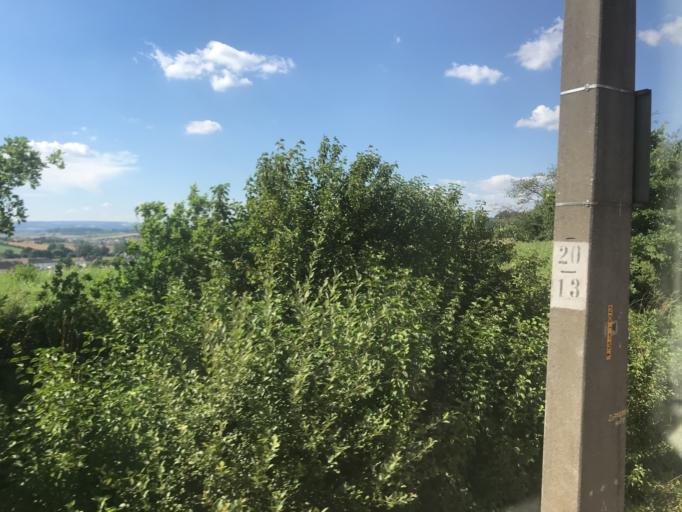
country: AT
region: Upper Austria
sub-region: Politischer Bezirk Urfahr-Umgebung
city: Engerwitzdorf
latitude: 48.3014
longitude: 14.4896
